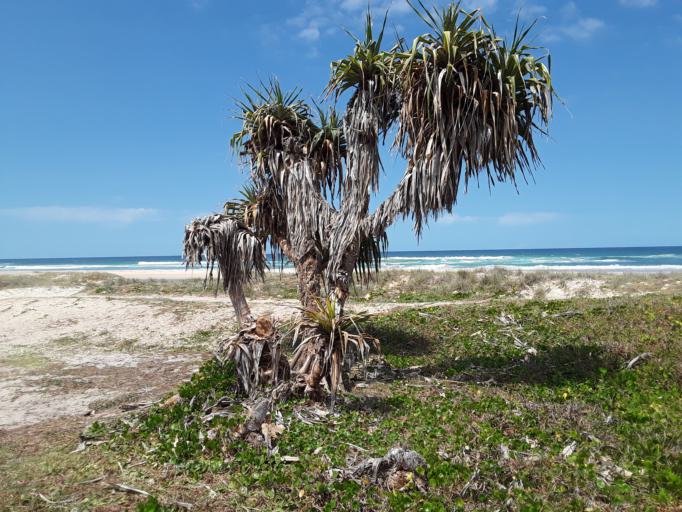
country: AU
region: Queensland
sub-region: Fraser Coast
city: Urangan
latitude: -25.2783
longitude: 153.2319
